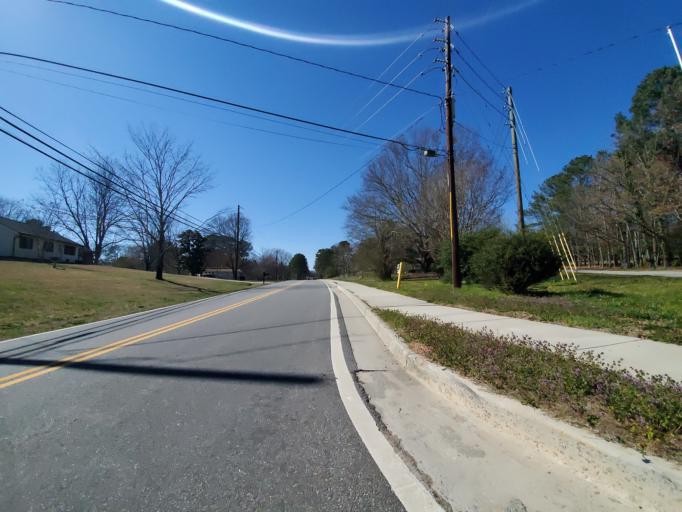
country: US
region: Georgia
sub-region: Gwinnett County
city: Dacula
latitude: 33.9826
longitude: -83.8834
